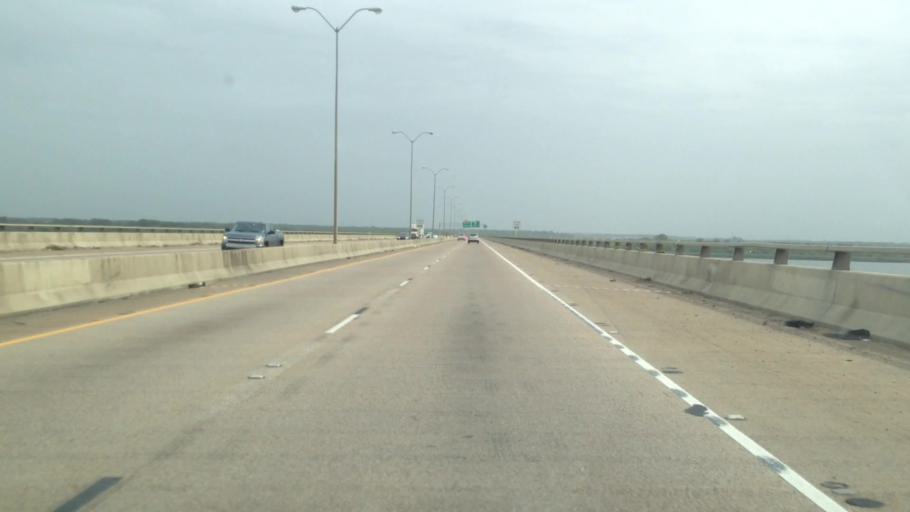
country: US
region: Louisiana
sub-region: Caddo Parish
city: Shreveport
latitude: 32.5105
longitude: -93.8136
